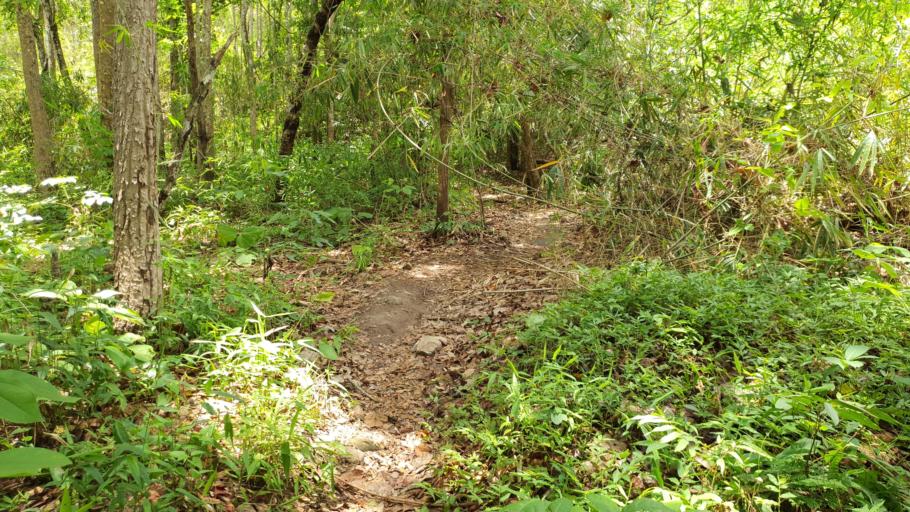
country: TH
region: Chiang Mai
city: San Sai
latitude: 18.9420
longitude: 99.0668
